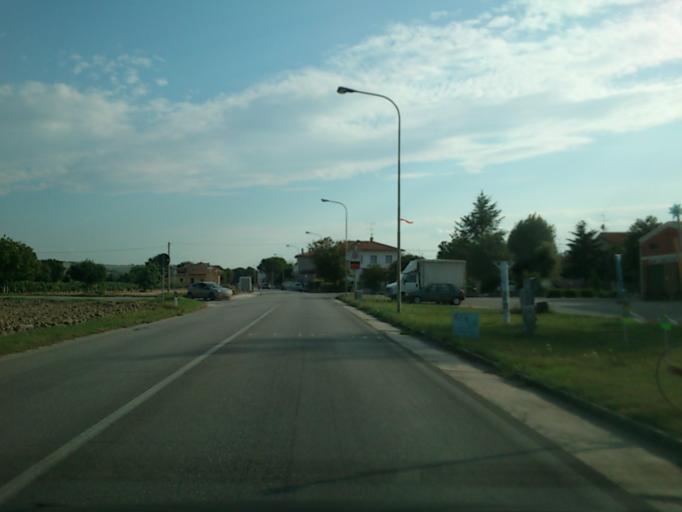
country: IT
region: The Marches
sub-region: Provincia di Pesaro e Urbino
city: Fano
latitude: 43.8218
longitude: 13.0528
